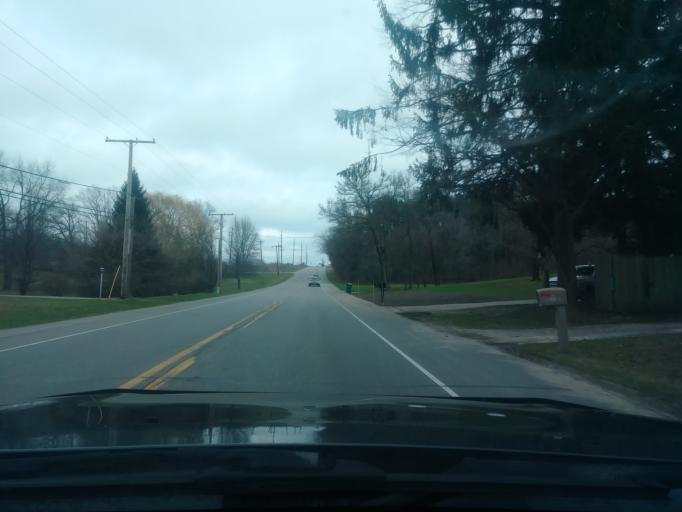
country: US
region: Indiana
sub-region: LaPorte County
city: Trail Creek
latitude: 41.6460
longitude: -86.8038
